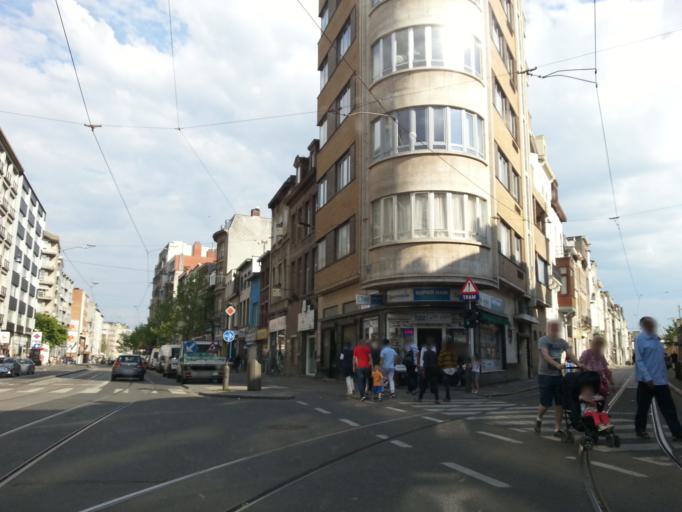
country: BE
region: Flanders
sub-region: Provincie Antwerpen
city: Antwerpen
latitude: 51.2186
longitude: 4.4240
